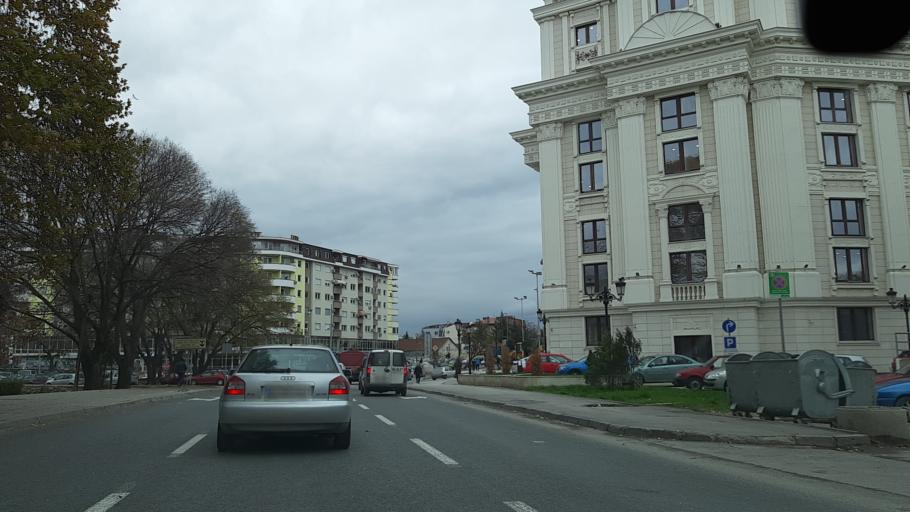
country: MK
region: Karpos
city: Skopje
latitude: 41.9886
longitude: 21.4311
